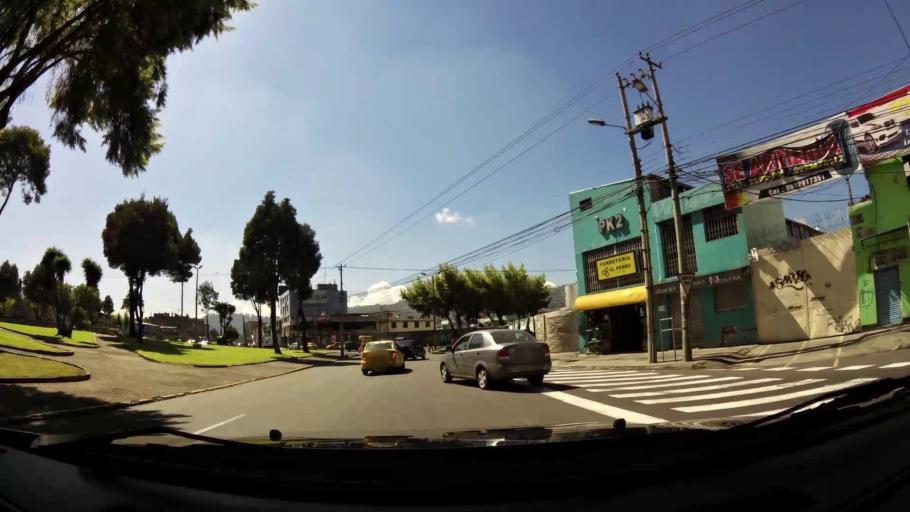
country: EC
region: Pichincha
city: Quito
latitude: -0.2499
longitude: -78.5314
